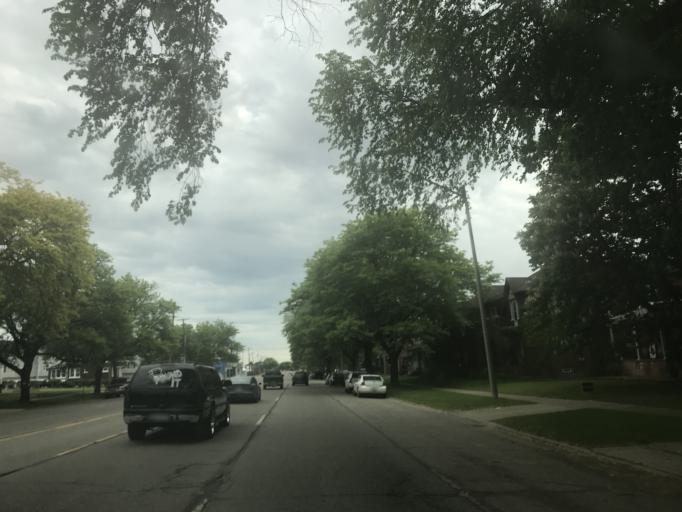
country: US
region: Michigan
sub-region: Wayne County
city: Ecorse
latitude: 42.2312
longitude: -83.1493
